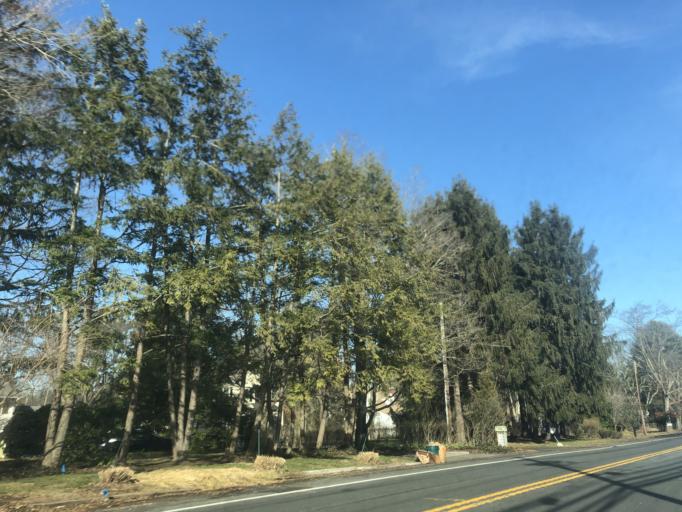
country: US
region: New Jersey
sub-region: Somerset County
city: Kingston
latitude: 40.3620
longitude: -74.6305
